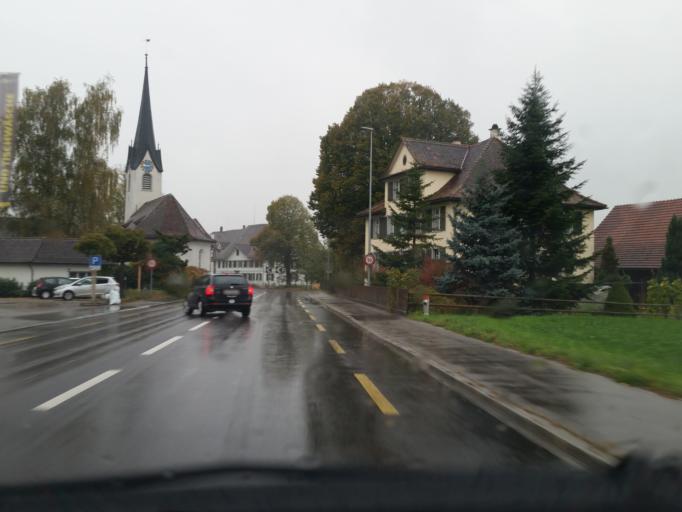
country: CH
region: Thurgau
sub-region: Weinfelden District
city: Erlen
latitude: 47.5478
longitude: 9.2362
